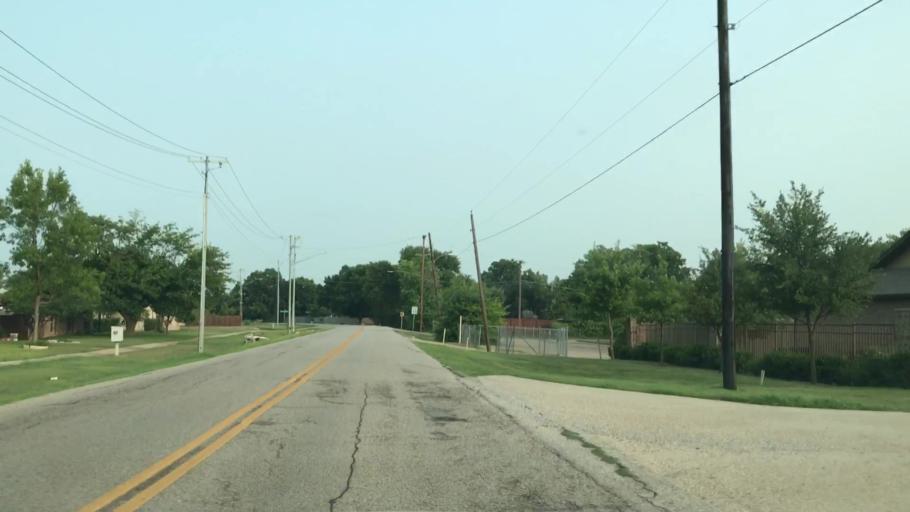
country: US
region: Texas
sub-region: Dallas County
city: Garland
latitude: 32.9205
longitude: -96.6071
